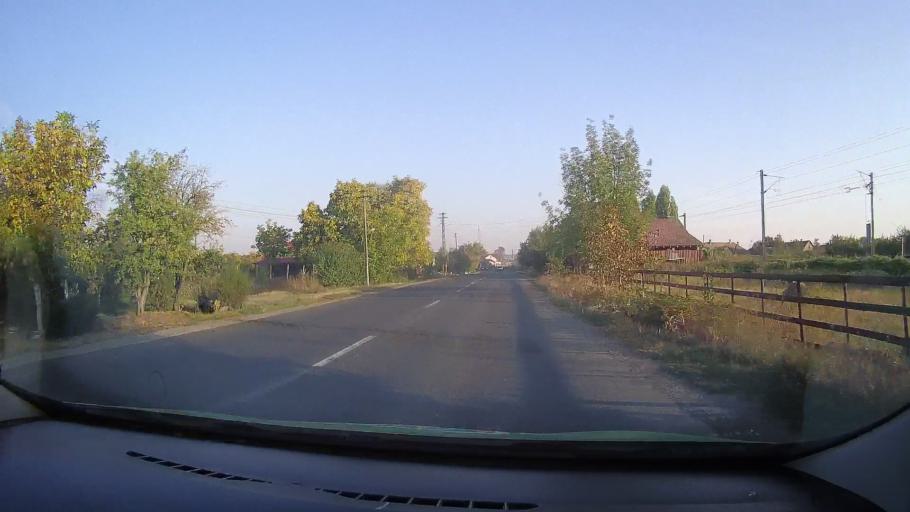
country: RO
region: Arad
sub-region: Comuna Sofronea
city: Sofronea
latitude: 46.2737
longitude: 21.3148
